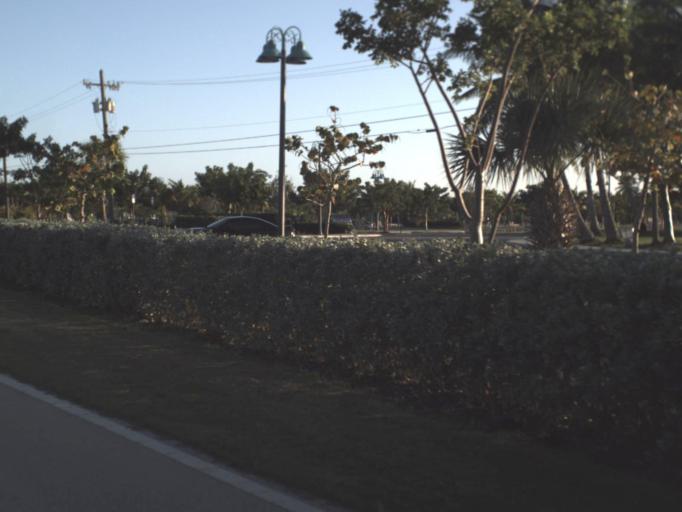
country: US
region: Florida
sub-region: Miami-Dade County
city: Key Biscayne
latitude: 25.7264
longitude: -80.1544
